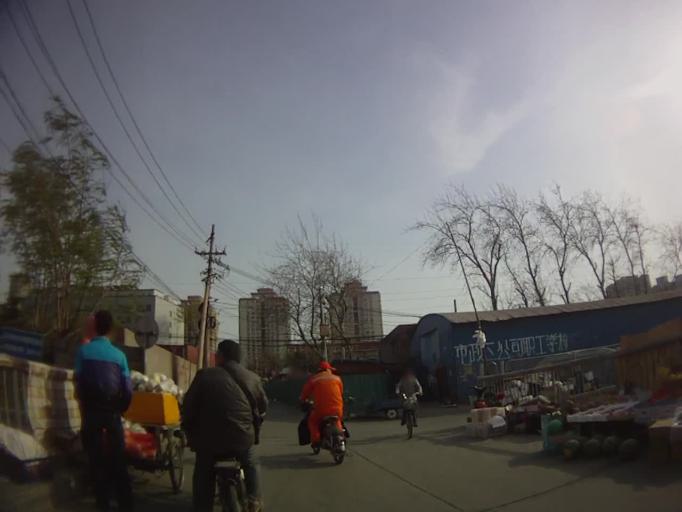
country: CN
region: Beijing
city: Chaowai
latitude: 39.9018
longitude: 116.4424
